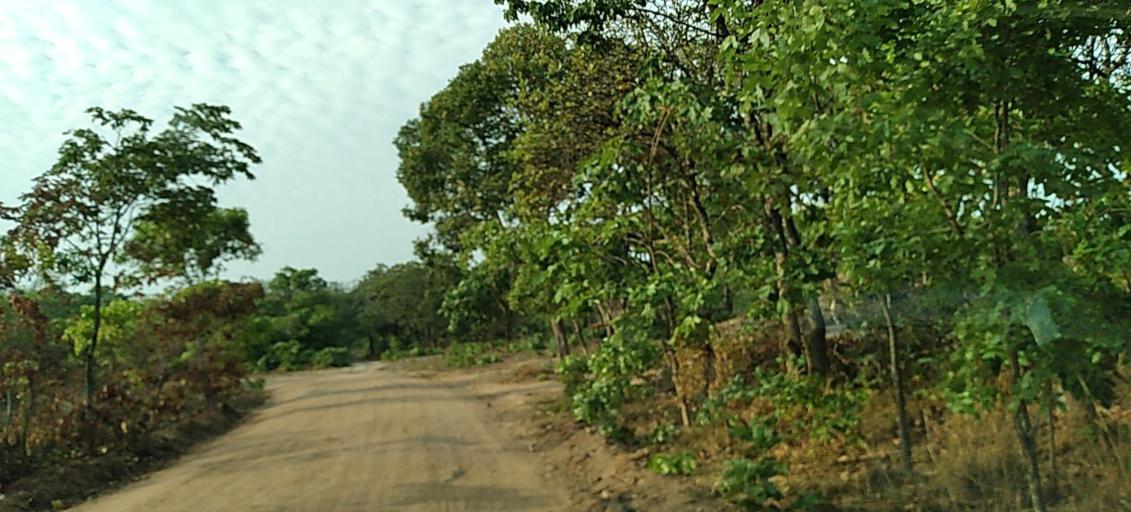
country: ZM
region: Copperbelt
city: Chingola
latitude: -12.8679
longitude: 27.6868
